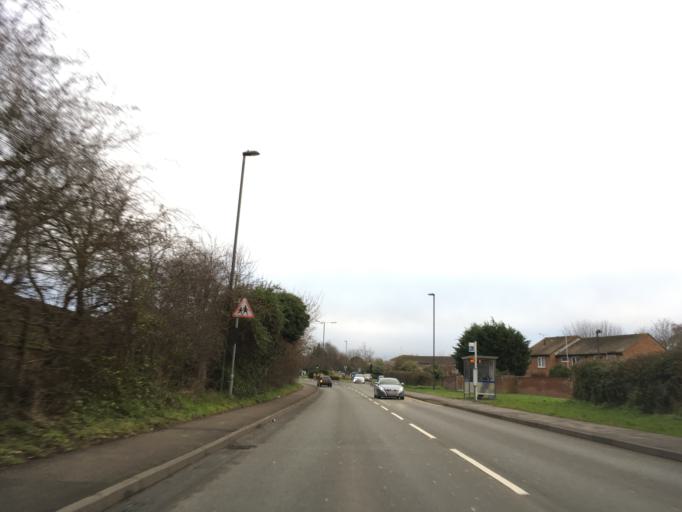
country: GB
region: England
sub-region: South Gloucestershire
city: Stoke Gifford
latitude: 51.5184
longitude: -2.5487
